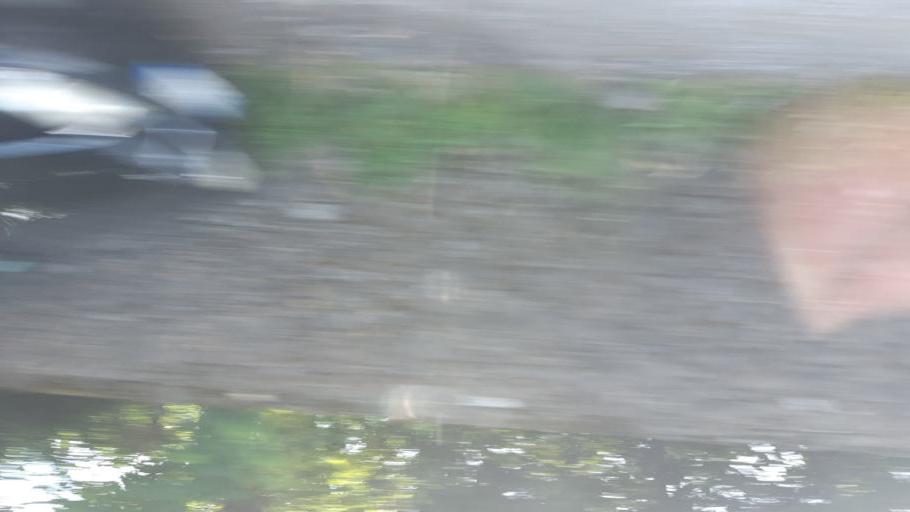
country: IT
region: Tuscany
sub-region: Provincia di Lucca
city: Capannori
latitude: 43.8682
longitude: 10.5655
